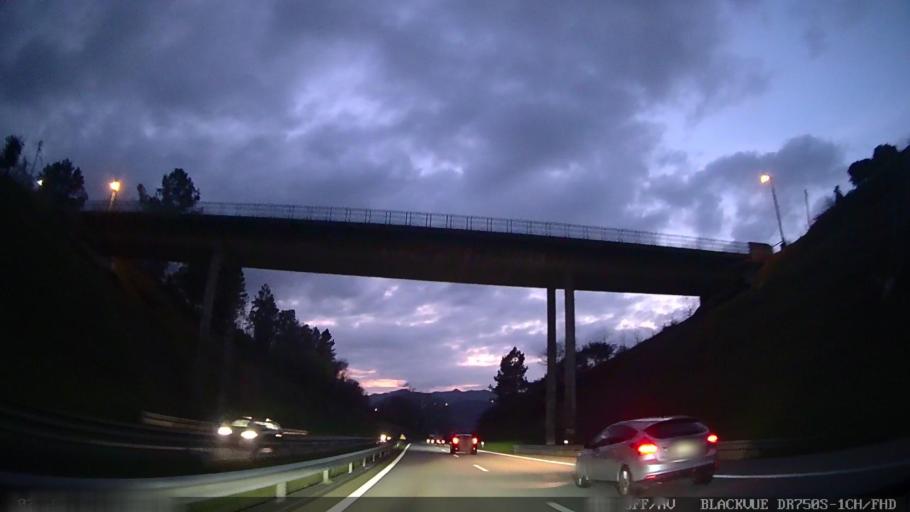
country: PT
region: Porto
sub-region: Amarante
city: Amarante
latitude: 41.2599
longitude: -8.0831
